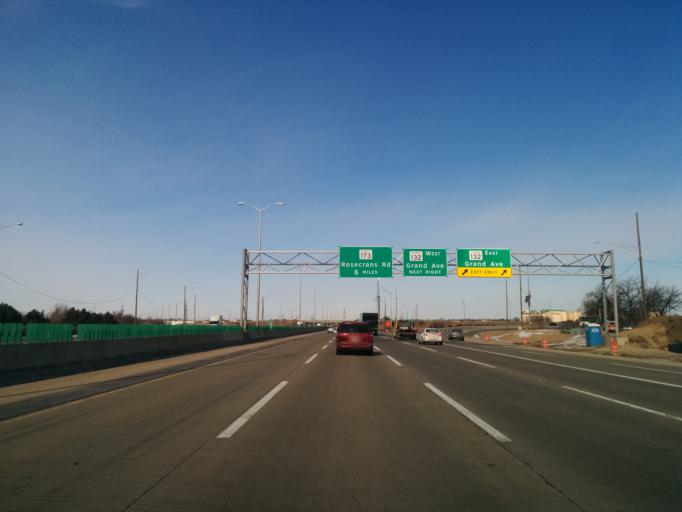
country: US
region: Illinois
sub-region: Lake County
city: Gurnee
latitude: 42.3762
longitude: -87.9450
